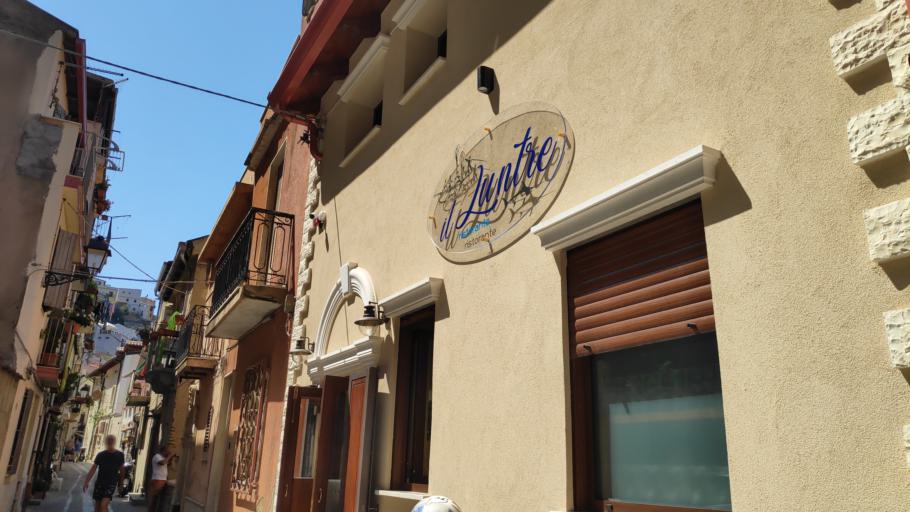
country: IT
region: Calabria
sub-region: Provincia di Reggio Calabria
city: Scilla
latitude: 38.2537
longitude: 15.7190
